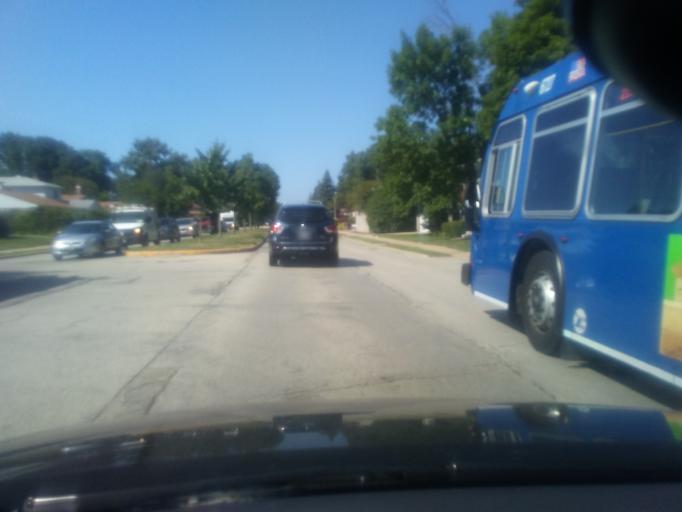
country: US
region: Illinois
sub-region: Cook County
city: Skokie
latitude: 42.0416
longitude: -87.7277
